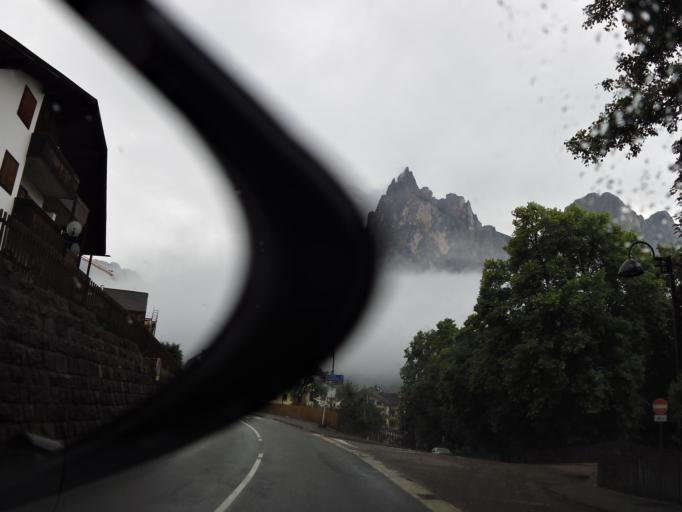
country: IT
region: Trentino-Alto Adige
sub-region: Bolzano
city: Siusi
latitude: 46.5471
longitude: 11.5591
